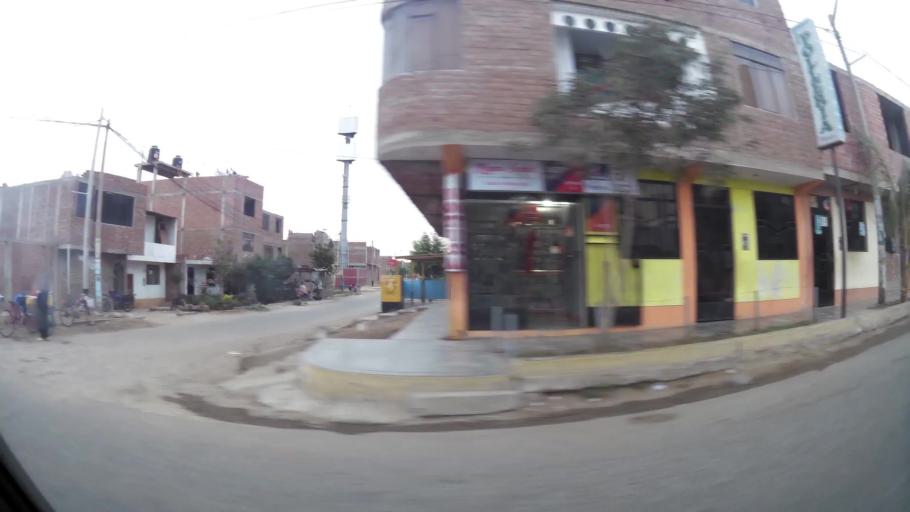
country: PE
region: La Libertad
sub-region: Provincia de Trujillo
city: El Porvenir
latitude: -8.0758
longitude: -79.0204
